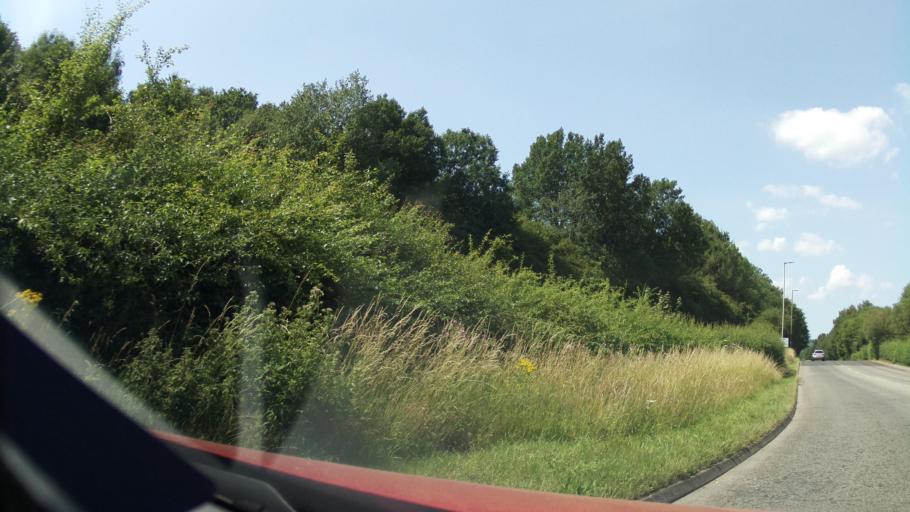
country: GB
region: Wales
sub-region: Caerphilly County Borough
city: Hengoed
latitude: 51.6500
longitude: -3.2224
